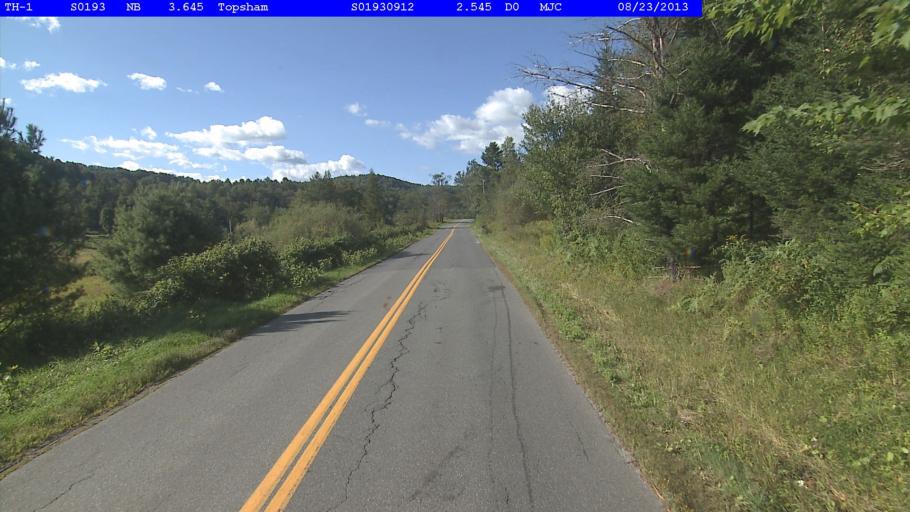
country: US
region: New Hampshire
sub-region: Grafton County
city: Haverhill
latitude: 44.1042
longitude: -72.2318
